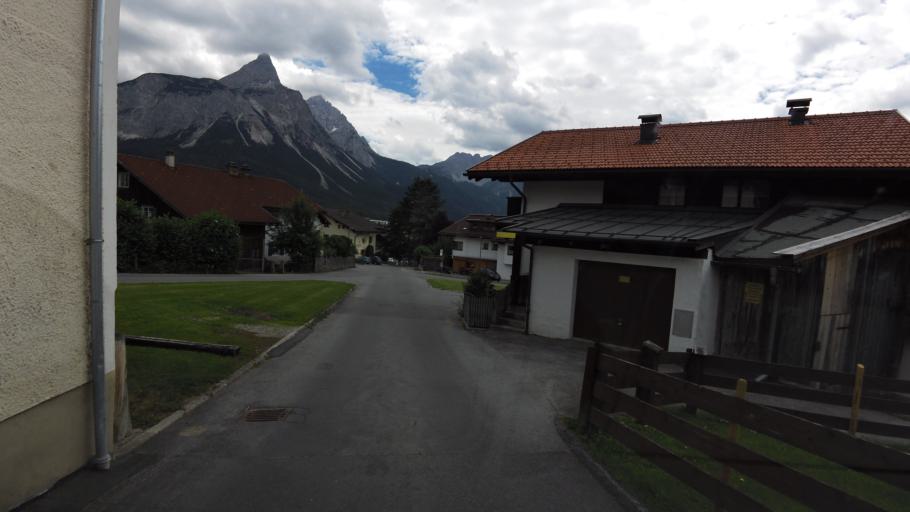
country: AT
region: Tyrol
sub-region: Politischer Bezirk Reutte
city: Ehrwald
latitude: 47.4068
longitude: 10.9192
